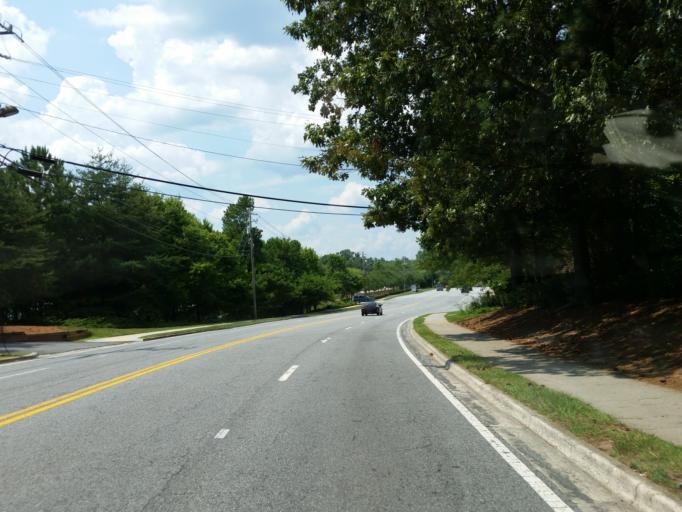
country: US
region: Georgia
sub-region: Fulton County
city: Roswell
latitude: 33.9939
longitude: -84.3480
